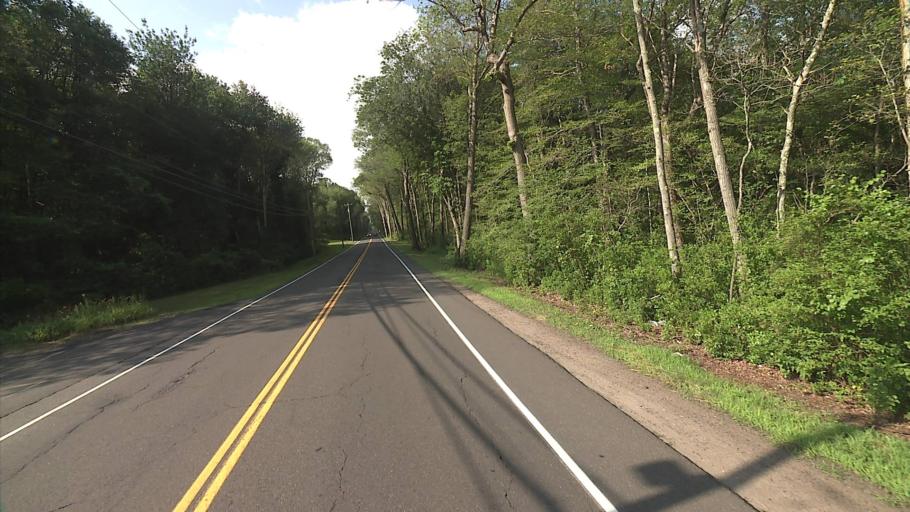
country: US
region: Connecticut
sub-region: Middlesex County
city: Higganum
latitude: 41.4287
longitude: -72.5605
